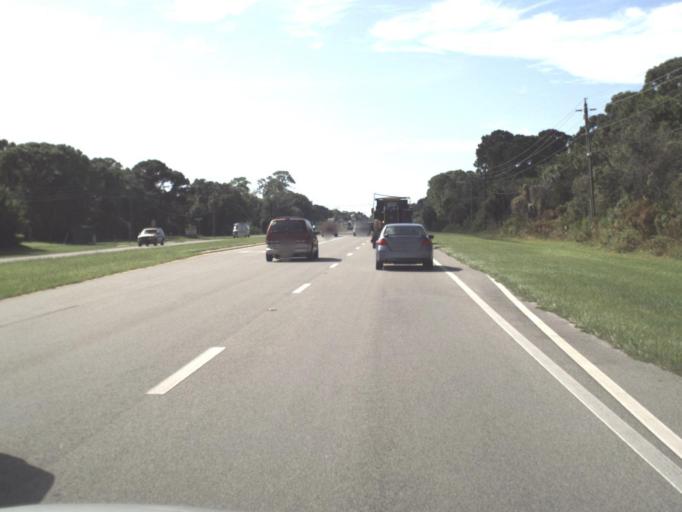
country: US
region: Florida
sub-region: Sarasota County
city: Vamo
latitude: 27.2124
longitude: -82.4904
